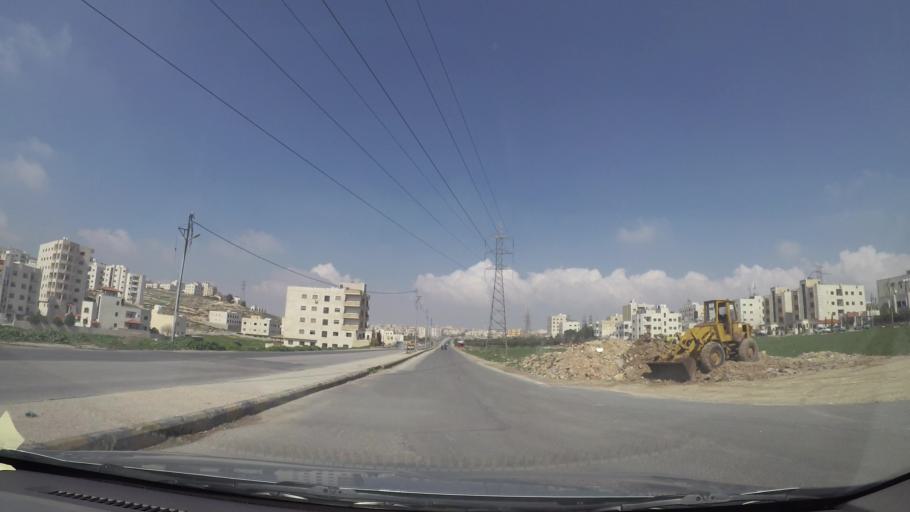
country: JO
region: Amman
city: Al Bunayyat ash Shamaliyah
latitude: 31.8890
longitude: 35.9025
